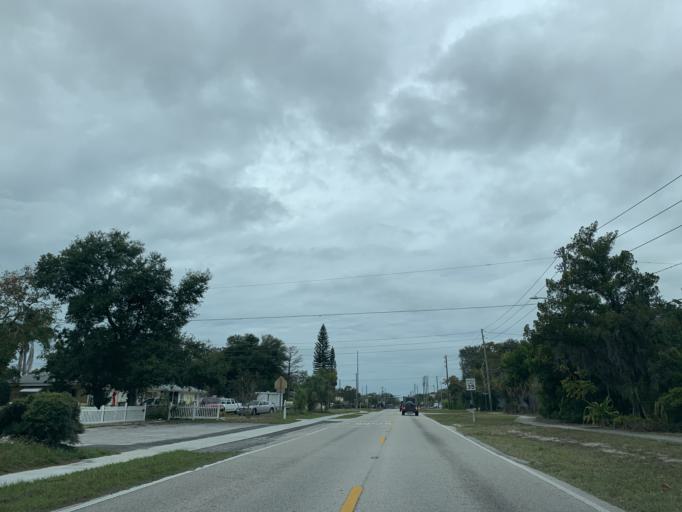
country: US
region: Florida
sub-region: Pinellas County
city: Belleair
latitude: 27.9389
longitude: -82.7844
